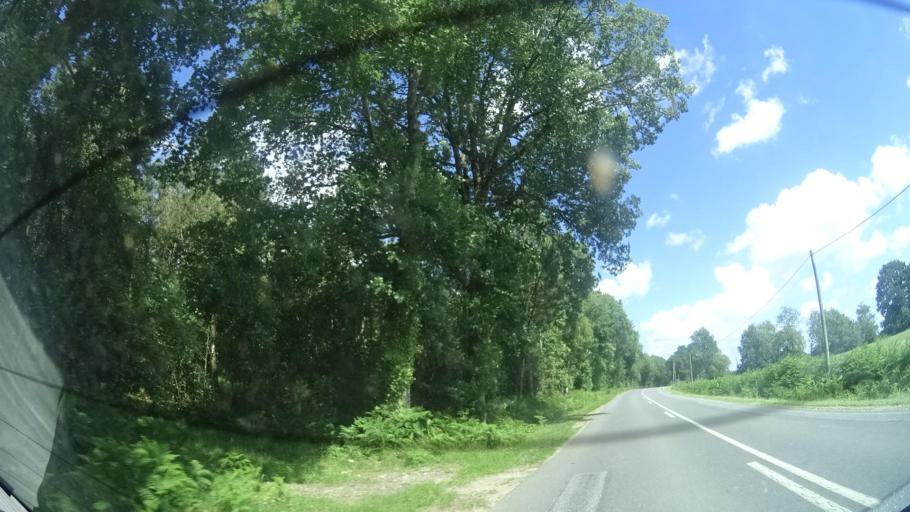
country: FR
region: Brittany
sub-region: Departement du Morbihan
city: Pluherlin
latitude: 47.6790
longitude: -2.3925
